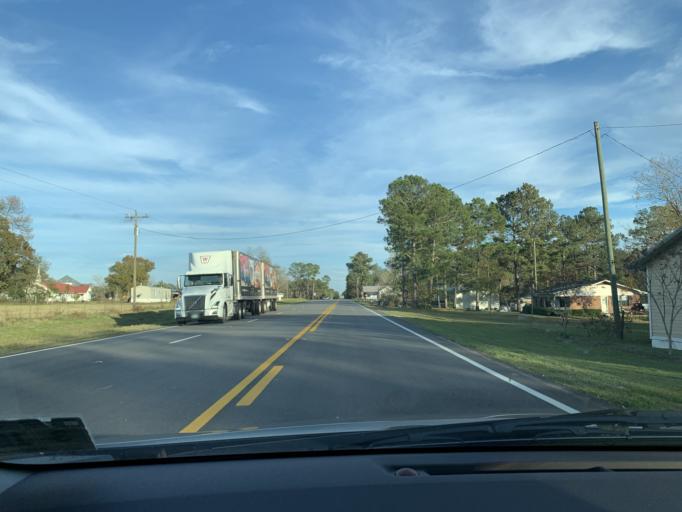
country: US
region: Georgia
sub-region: Irwin County
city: Ocilla
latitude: 31.5958
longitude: -83.1527
